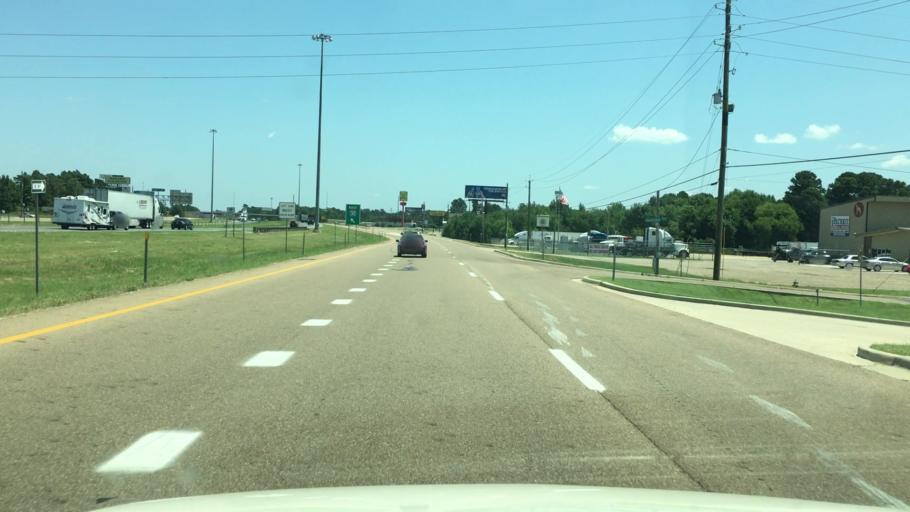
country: US
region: Arkansas
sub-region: Miller County
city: Texarkana
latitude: 33.4698
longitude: -94.0380
